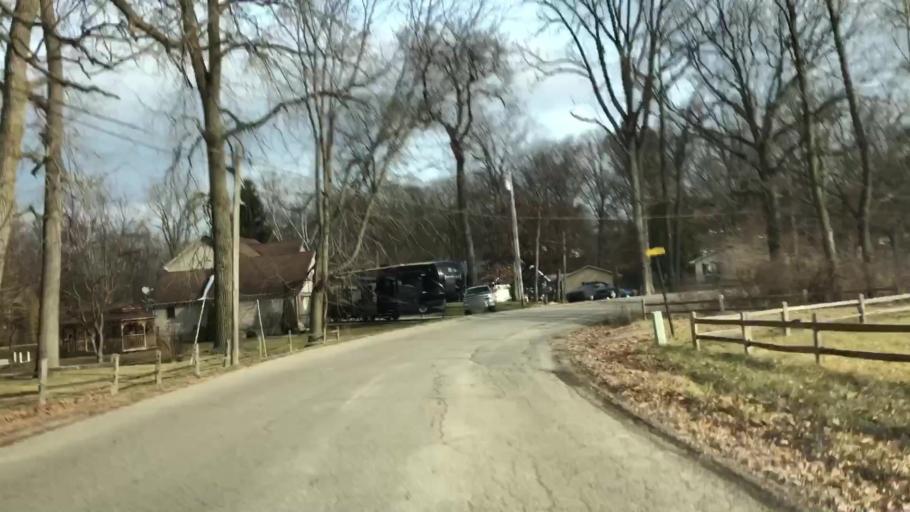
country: US
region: Indiana
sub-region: Steuben County
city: Angola
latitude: 41.6810
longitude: -85.0199
